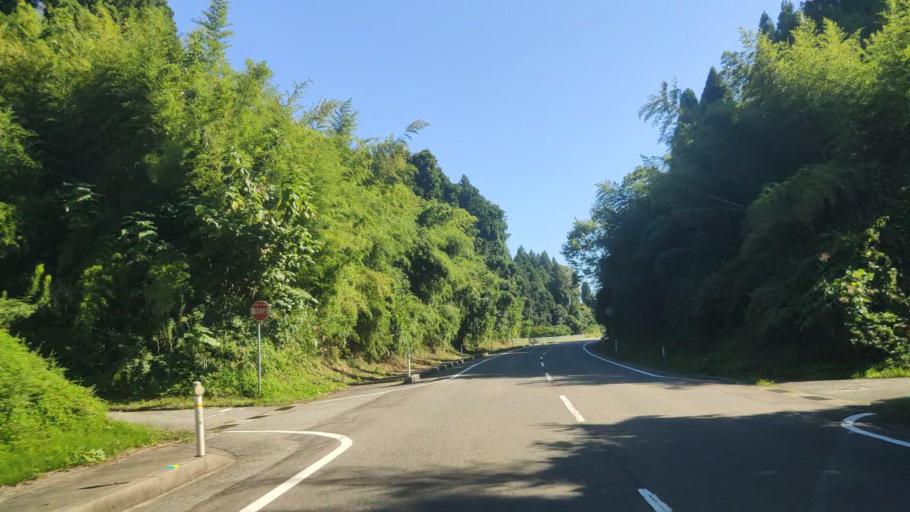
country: JP
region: Ishikawa
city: Nanao
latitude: 37.3760
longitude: 137.2340
